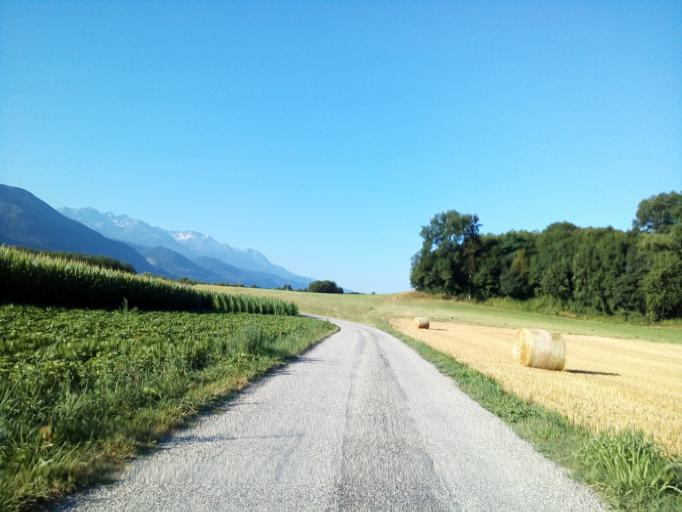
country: FR
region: Rhone-Alpes
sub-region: Departement de l'Isere
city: Saint-Vincent-de-Mercuze
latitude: 45.3712
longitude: 5.9703
